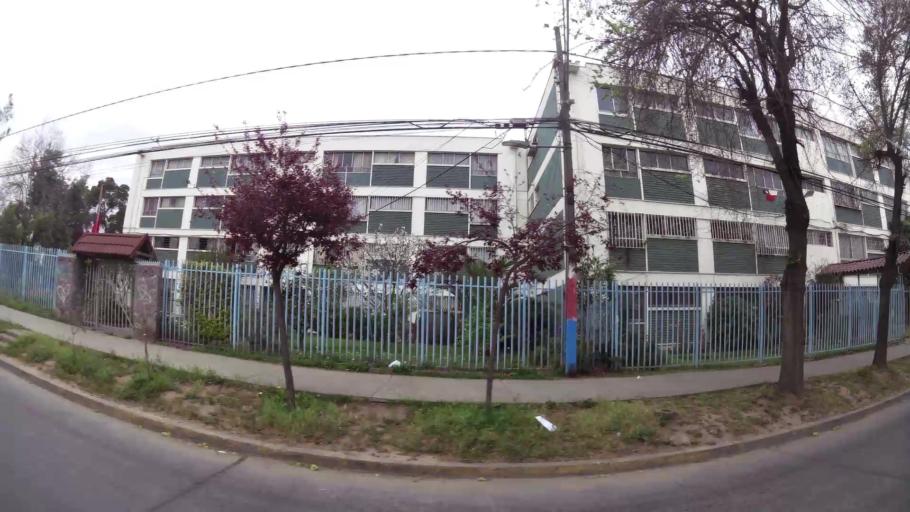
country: CL
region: Santiago Metropolitan
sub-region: Provincia de Santiago
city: Villa Presidente Frei, Nunoa, Santiago, Chile
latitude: -33.4749
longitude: -70.5876
